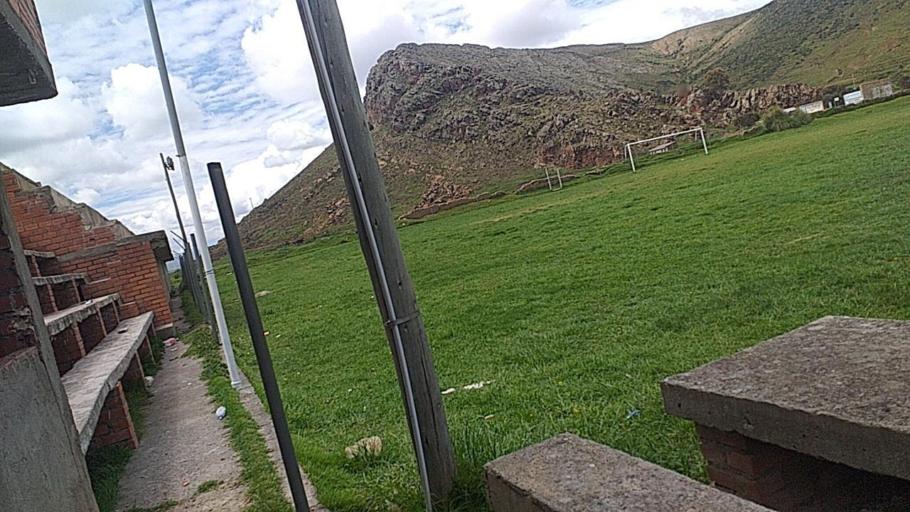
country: BO
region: La Paz
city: Batallas
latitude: -16.3484
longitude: -68.6339
